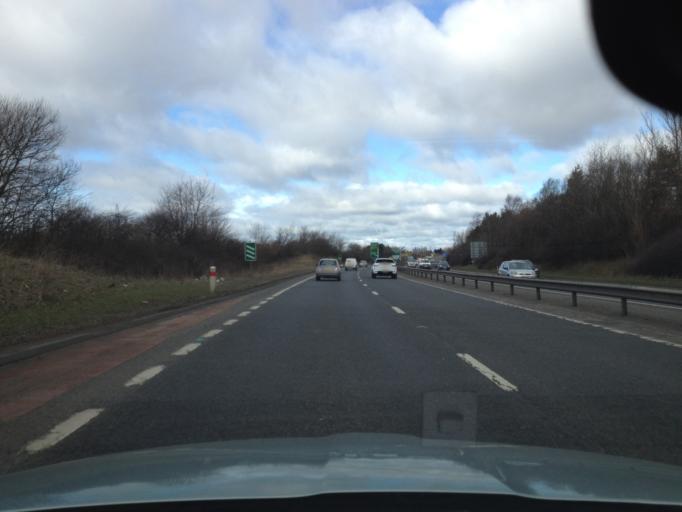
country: GB
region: Scotland
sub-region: Edinburgh
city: Currie
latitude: 55.9146
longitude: -3.2962
